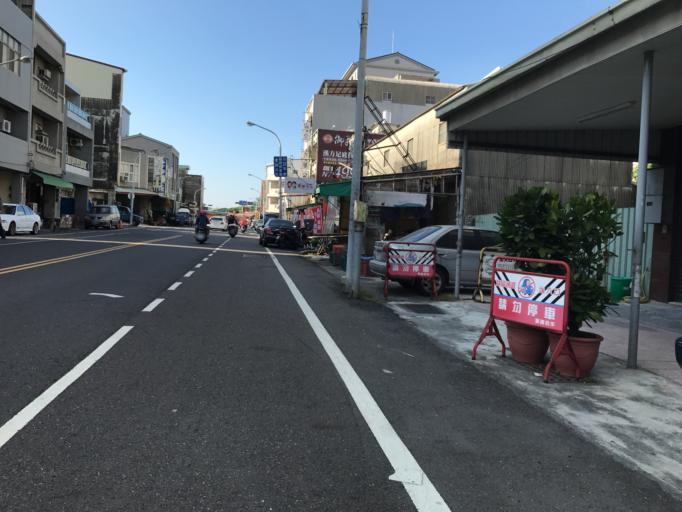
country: TW
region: Taiwan
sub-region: Tainan
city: Tainan
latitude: 23.0012
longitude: 120.1660
